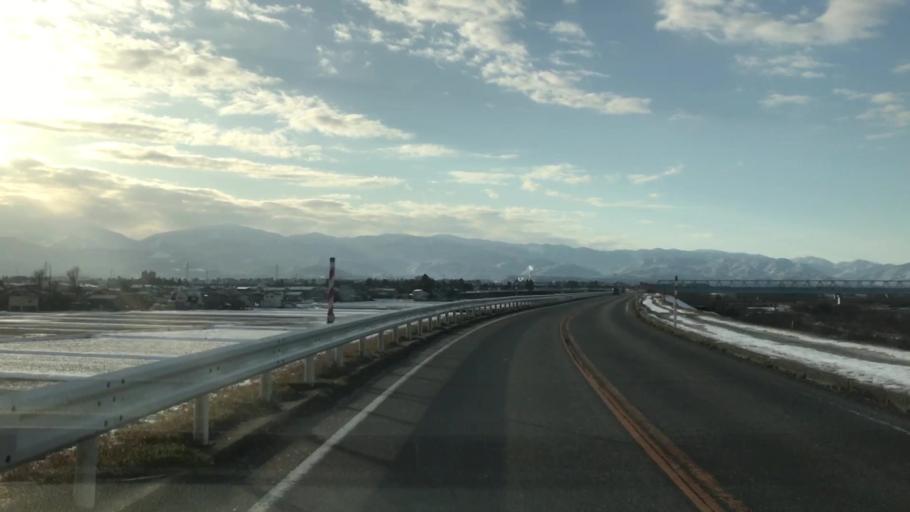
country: JP
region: Toyama
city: Toyama-shi
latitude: 36.6778
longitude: 137.2851
